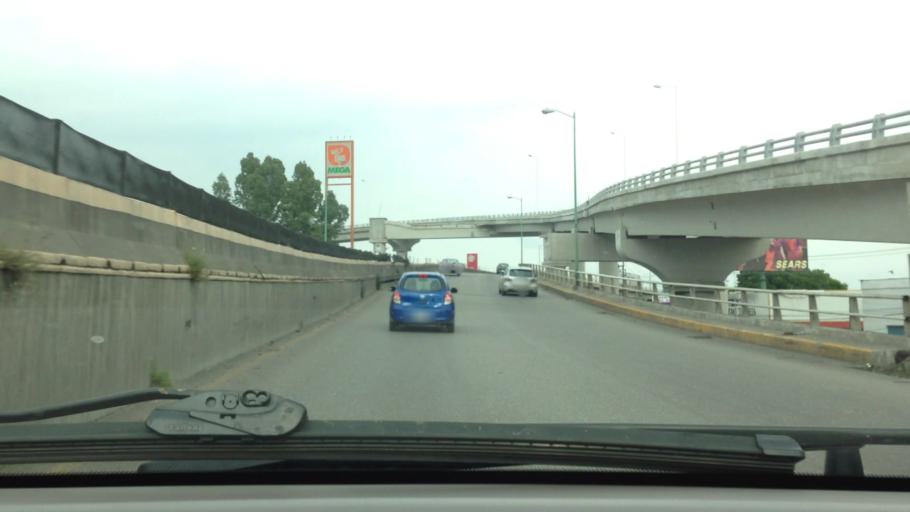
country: MX
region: Morelos
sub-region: Tepoztlan
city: Loma Bonita
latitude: 18.9209
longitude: -99.2014
